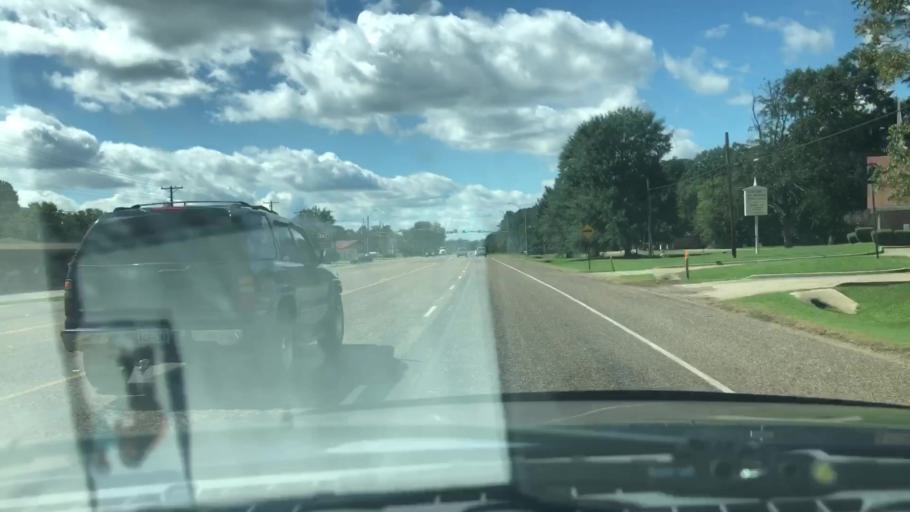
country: US
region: Texas
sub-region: Bowie County
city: Wake Village
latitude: 33.4018
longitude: -94.0785
